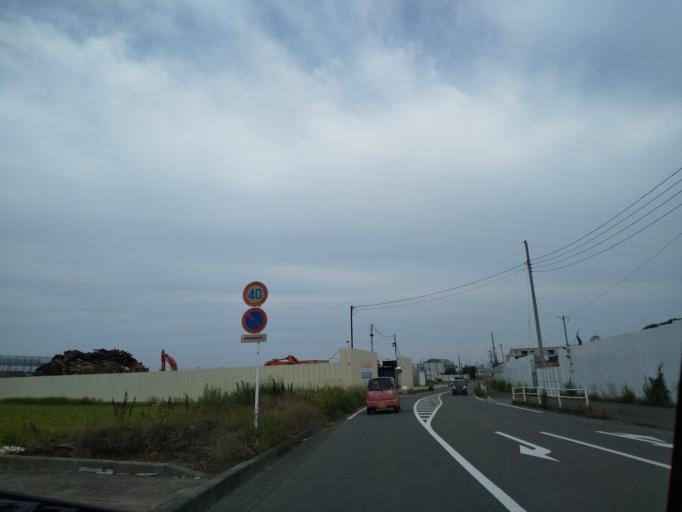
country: JP
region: Kanagawa
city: Atsugi
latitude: 35.4760
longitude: 139.3527
